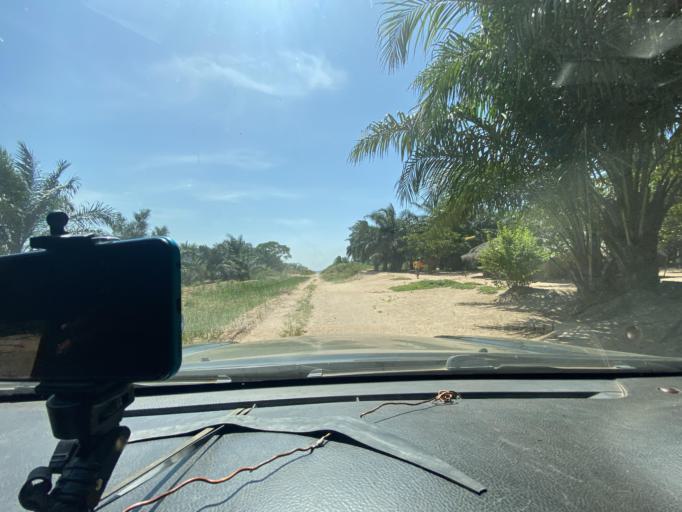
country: CD
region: Kasai-Oriental
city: Kabinda
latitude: -5.9514
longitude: 24.8045
